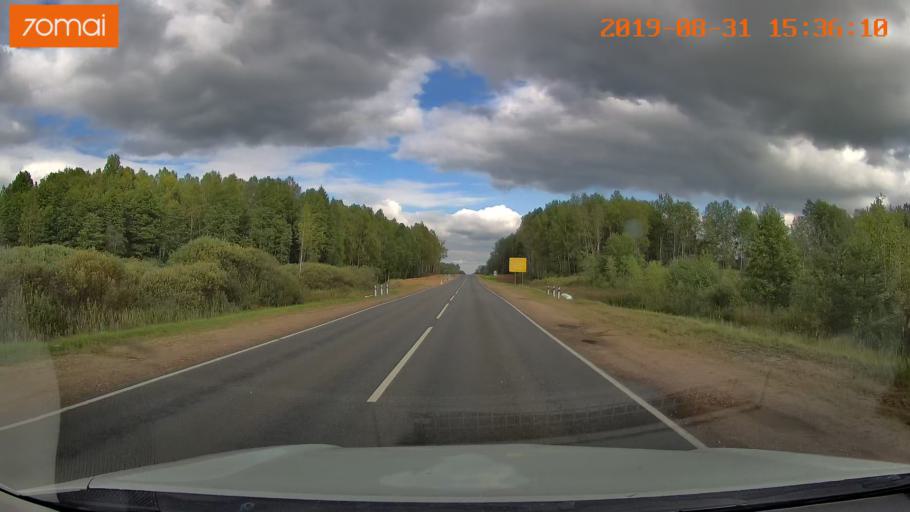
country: RU
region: Kaluga
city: Mosal'sk
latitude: 54.6094
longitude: 34.7522
